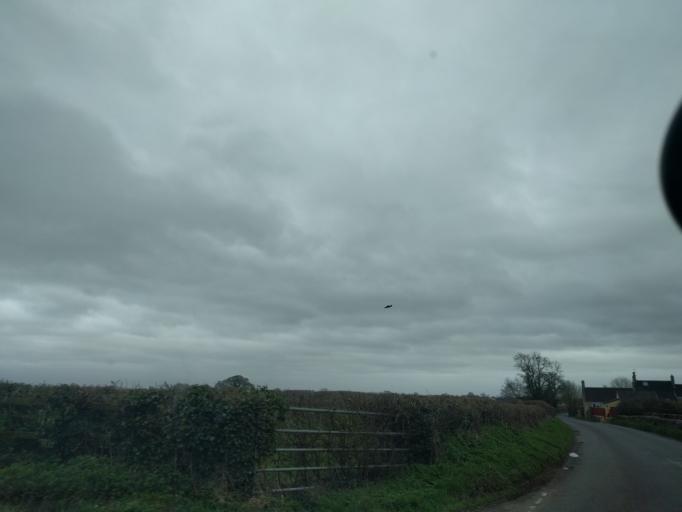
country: GB
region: England
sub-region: Wiltshire
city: Biddestone
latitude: 51.4972
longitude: -2.1946
